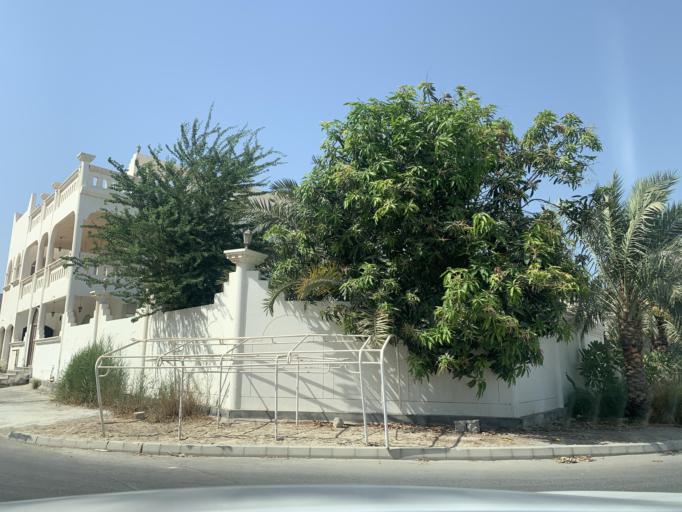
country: BH
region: Manama
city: Jidd Hafs
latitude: 26.2278
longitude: 50.4609
